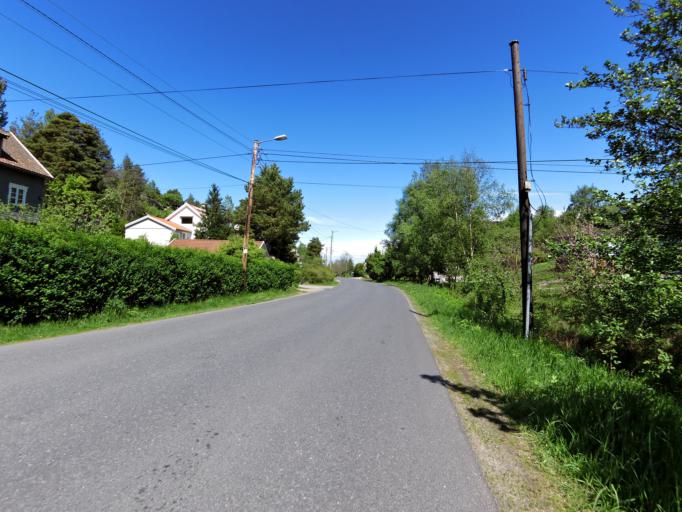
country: NO
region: Ostfold
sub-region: Fredrikstad
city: Fredrikstad
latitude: 59.2249
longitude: 10.9655
